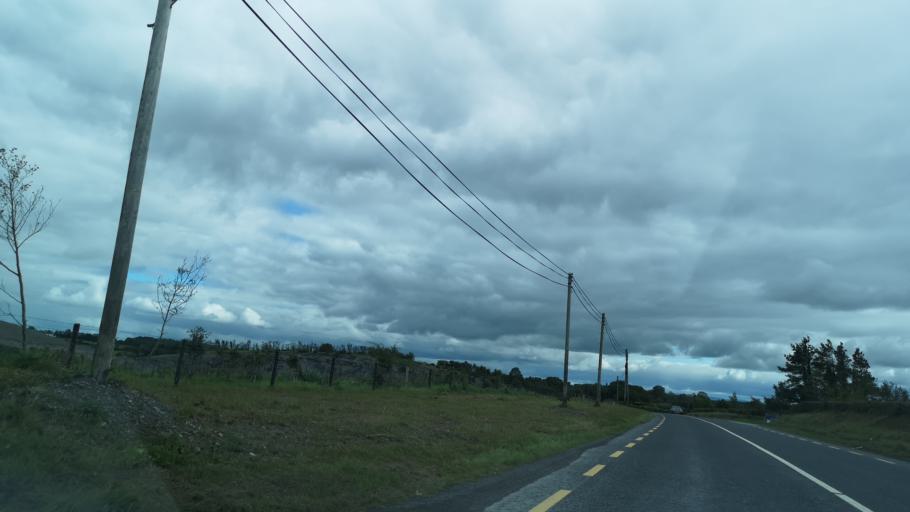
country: IE
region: Connaught
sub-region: County Galway
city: Ballinasloe
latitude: 53.3050
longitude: -8.1406
